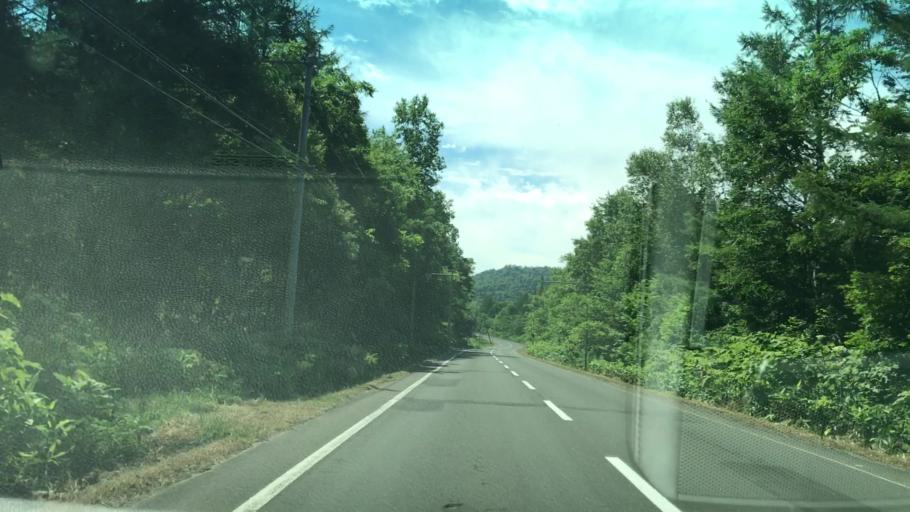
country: JP
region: Hokkaido
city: Shimo-furano
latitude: 42.9618
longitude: 142.4282
